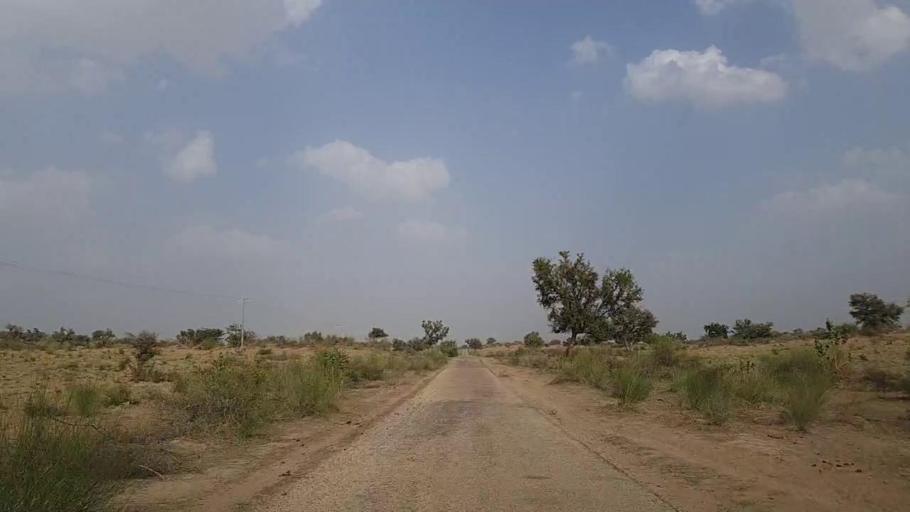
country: PK
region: Sindh
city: Islamkot
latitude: 24.8697
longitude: 70.1242
